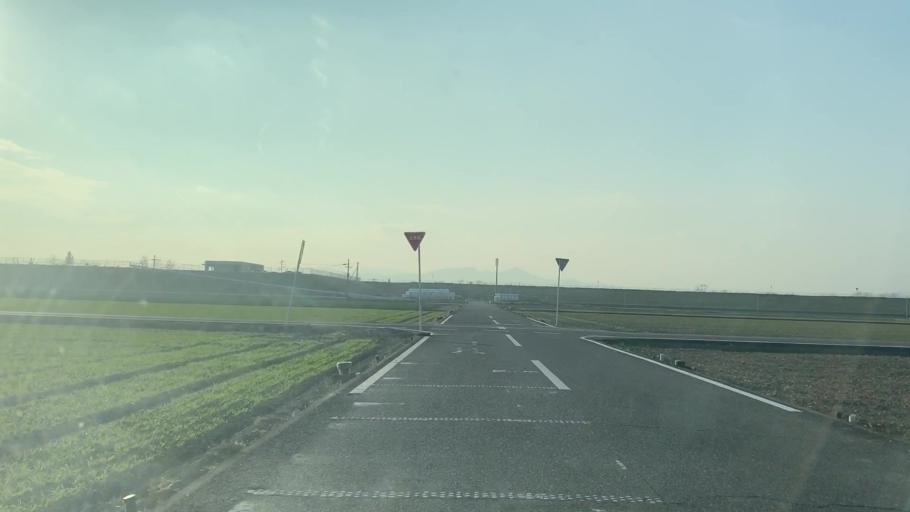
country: JP
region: Saga Prefecture
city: Saga-shi
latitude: 33.2600
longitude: 130.2486
